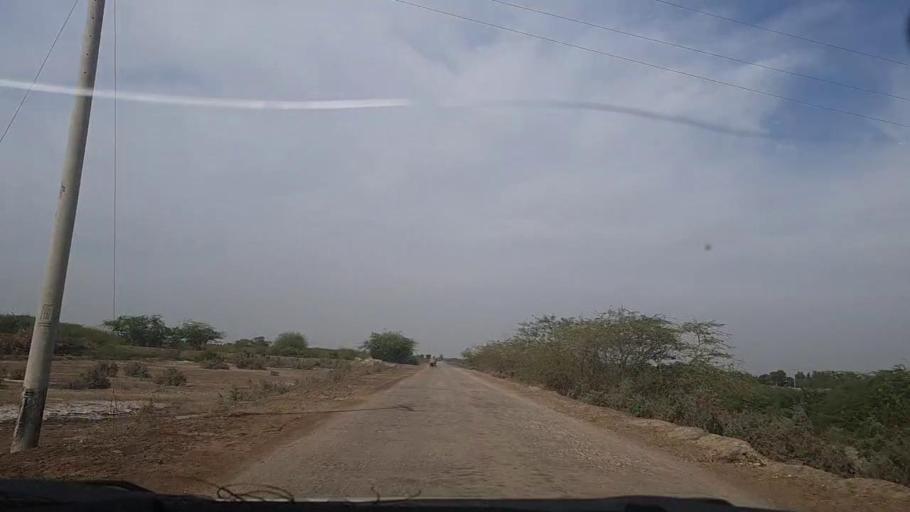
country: PK
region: Sindh
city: Pithoro
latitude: 25.5403
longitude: 69.3606
